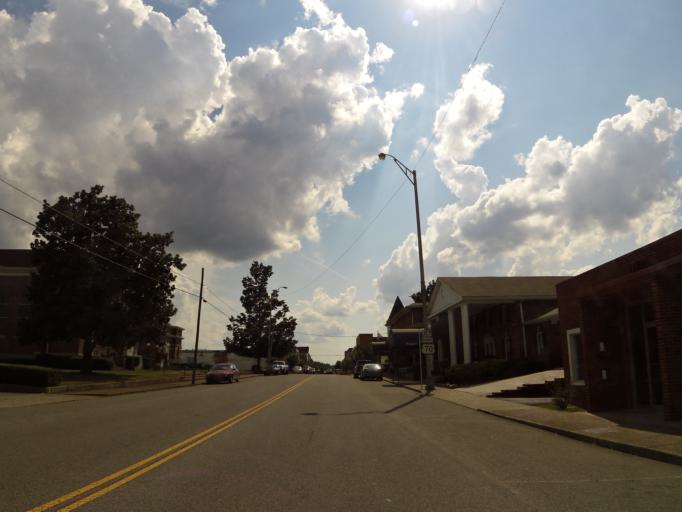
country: US
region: Tennessee
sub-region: Dickson County
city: Dickson
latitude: 36.0779
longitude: -87.3862
